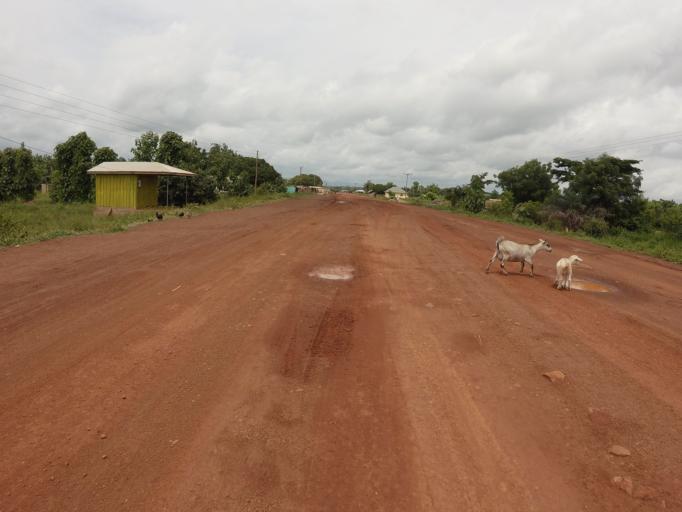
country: GH
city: Kpandae
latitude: 8.4027
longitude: 0.4021
